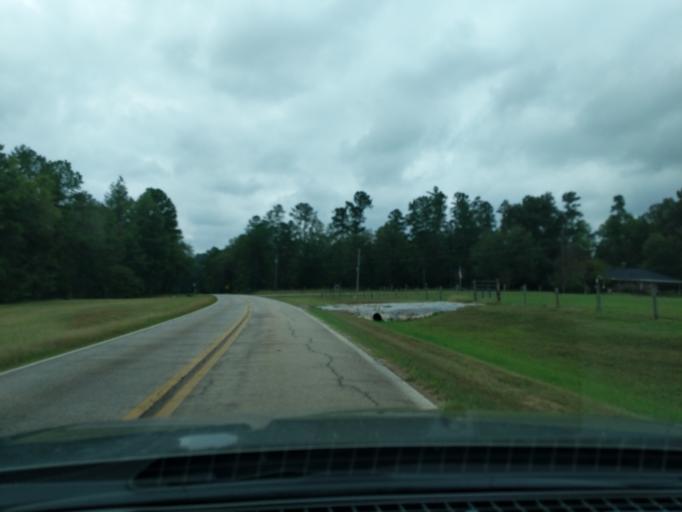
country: US
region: Georgia
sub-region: Columbia County
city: Appling
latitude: 33.5768
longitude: -82.3693
